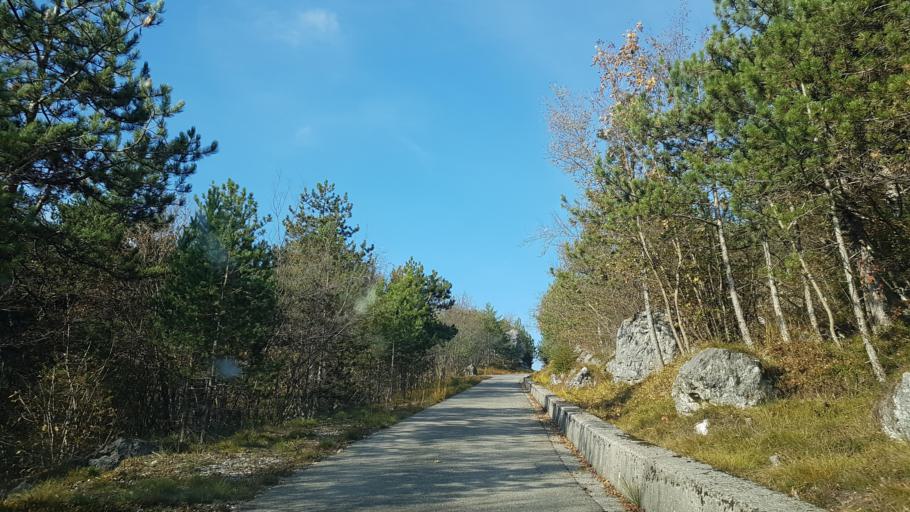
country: IT
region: Friuli Venezia Giulia
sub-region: Provincia di Udine
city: Moggio Udinese
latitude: 46.4406
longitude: 13.2043
